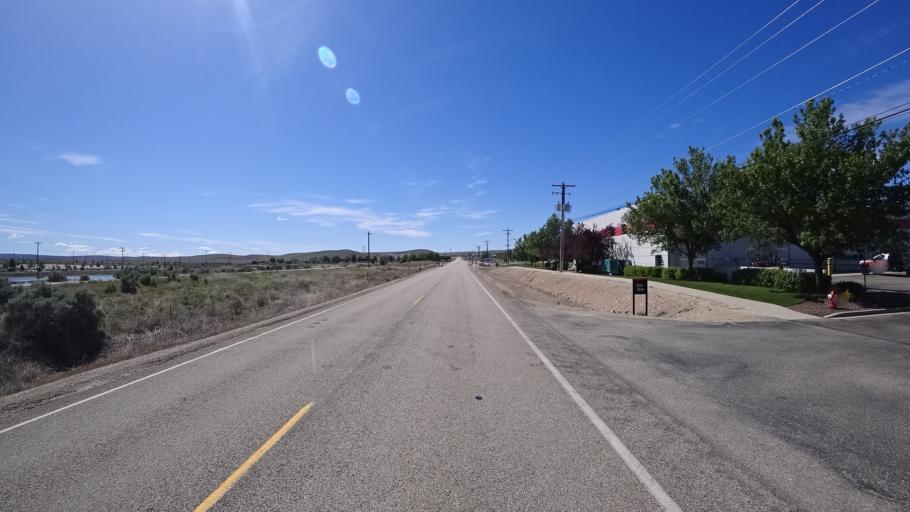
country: US
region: Idaho
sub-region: Ada County
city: Boise
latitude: 43.5219
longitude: -116.1472
